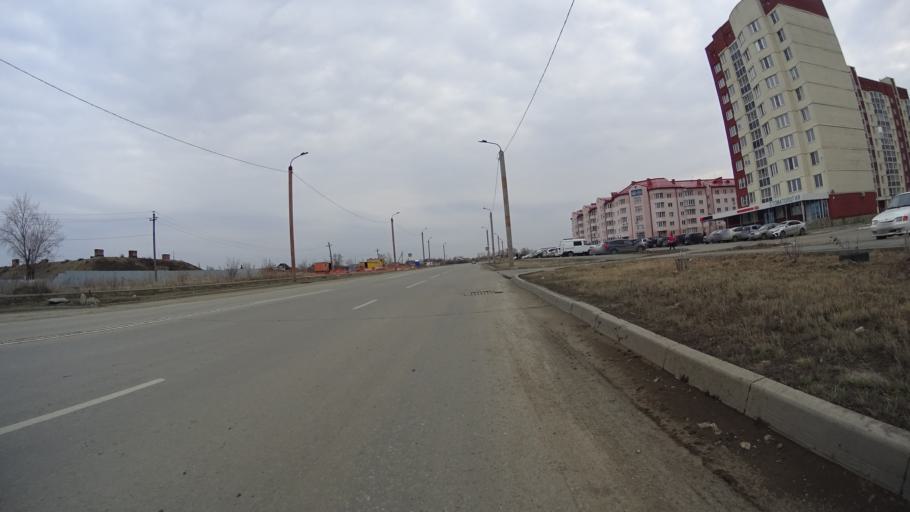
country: RU
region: Chelyabinsk
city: Zheleznodorozhnyy
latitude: 55.1700
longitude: 61.5375
